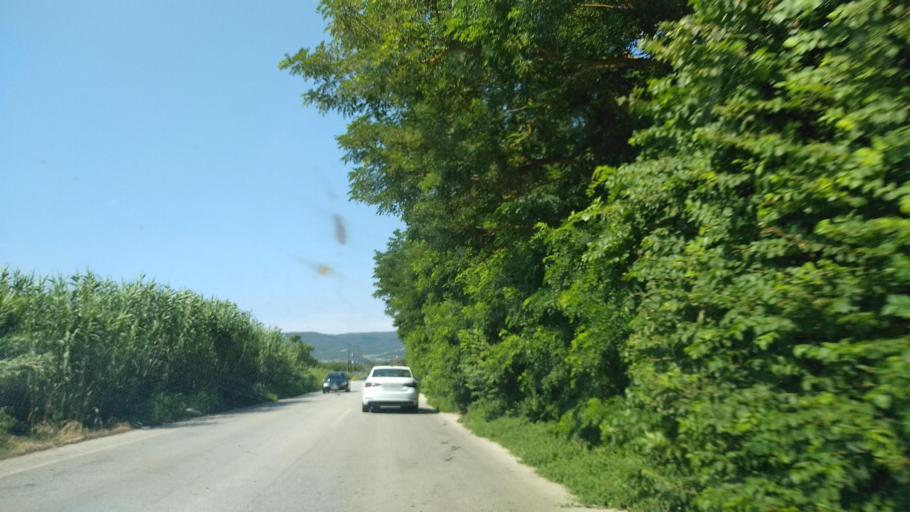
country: GR
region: Central Macedonia
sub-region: Nomos Thessalonikis
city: Stavros
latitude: 40.6500
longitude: 23.6055
